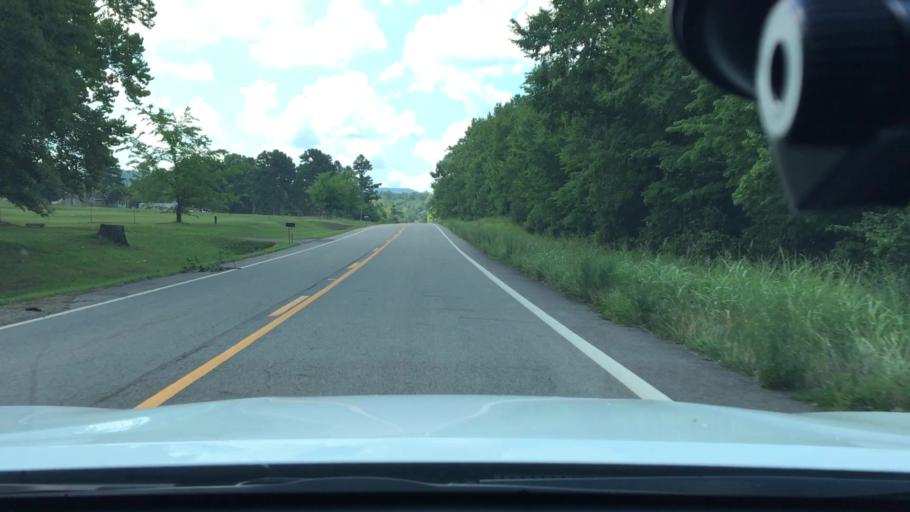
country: US
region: Arkansas
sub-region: Logan County
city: Paris
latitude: 35.2657
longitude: -93.6832
